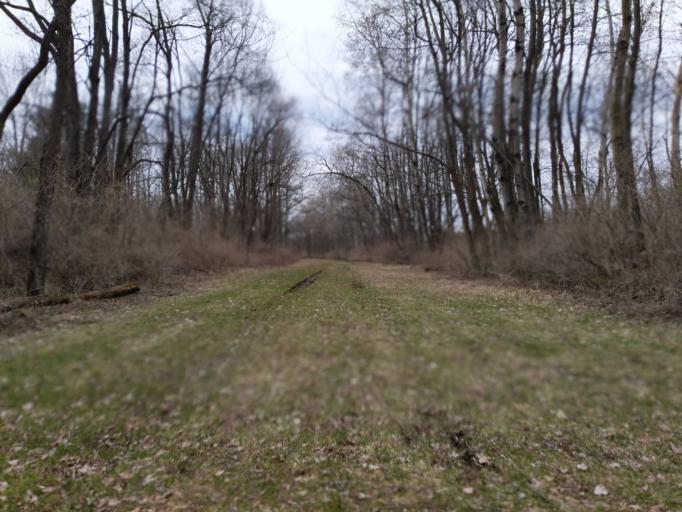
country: US
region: New York
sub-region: Tompkins County
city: Dryden
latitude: 42.4947
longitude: -76.3082
